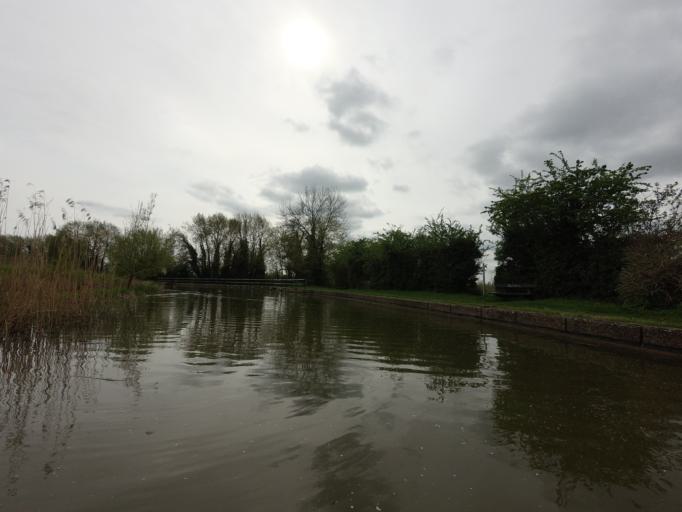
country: GB
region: England
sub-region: Milton Keynes
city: Bradwell
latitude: 52.0740
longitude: -0.7816
